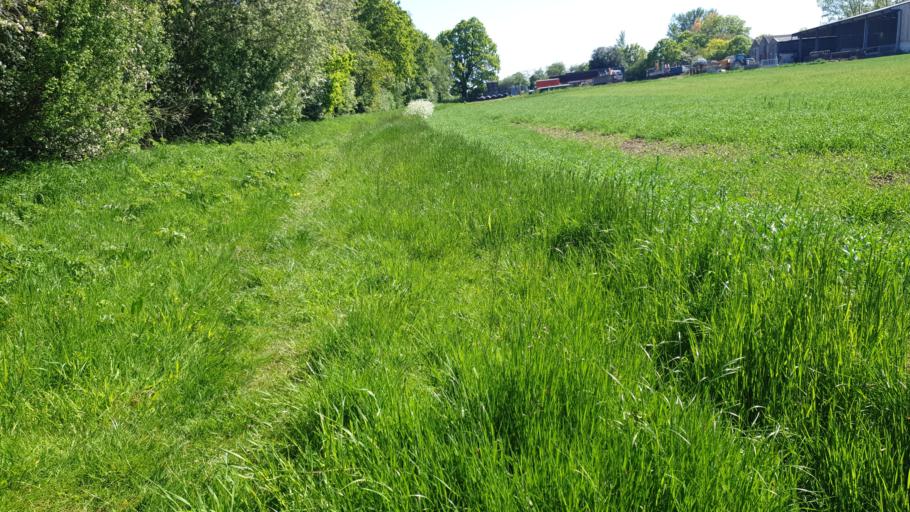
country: GB
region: England
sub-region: Essex
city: Great Bentley
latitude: 51.8590
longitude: 1.0513
